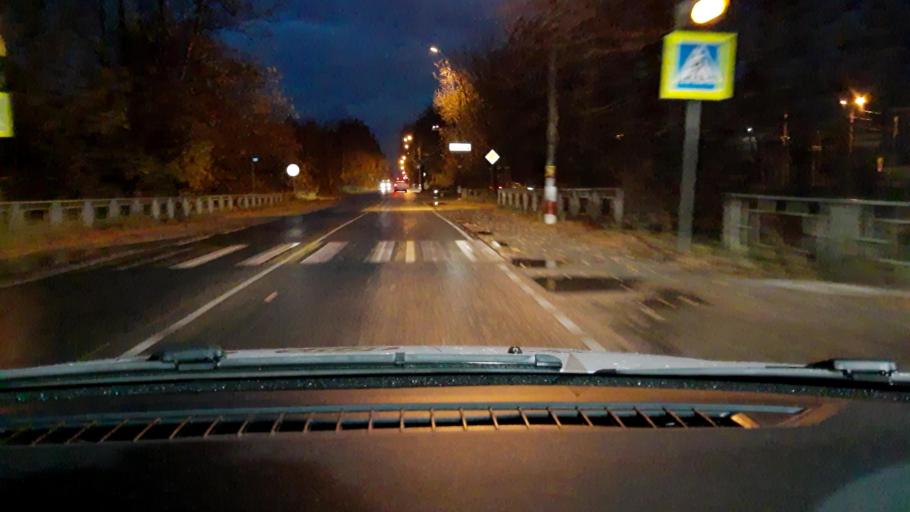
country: RU
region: Nizjnij Novgorod
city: Bor
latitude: 56.3604
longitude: 44.0889
